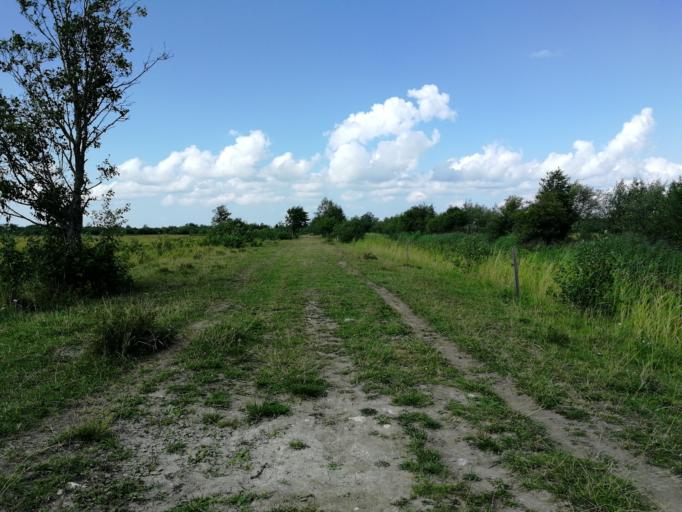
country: EE
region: Laeaene
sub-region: Lihula vald
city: Lihula
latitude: 58.7223
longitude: 23.8084
